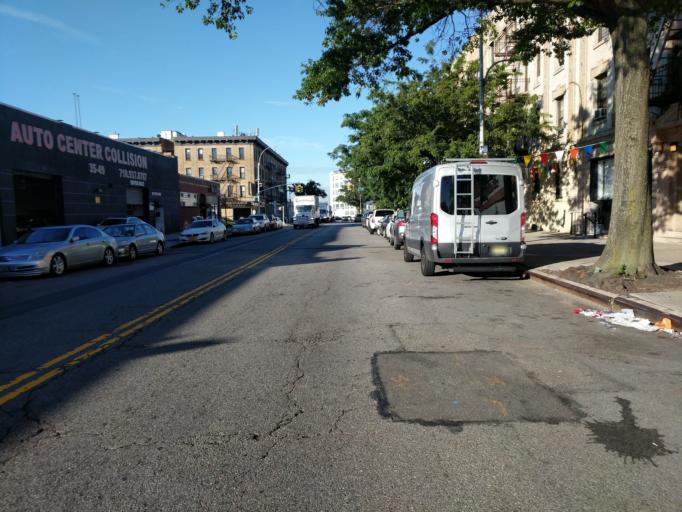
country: US
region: New York
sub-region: Queens County
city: Long Island City
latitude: 40.7542
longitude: -73.9229
